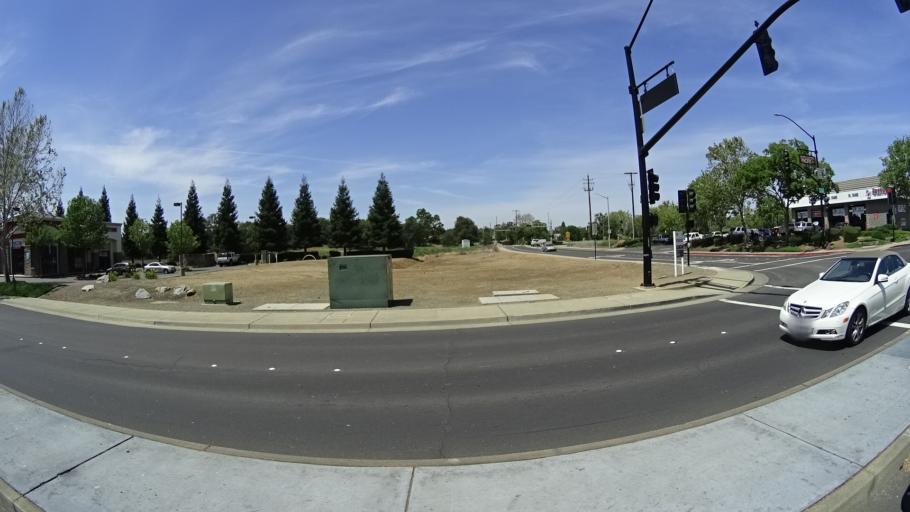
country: US
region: California
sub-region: Placer County
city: Rocklin
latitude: 38.7856
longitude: -121.2399
